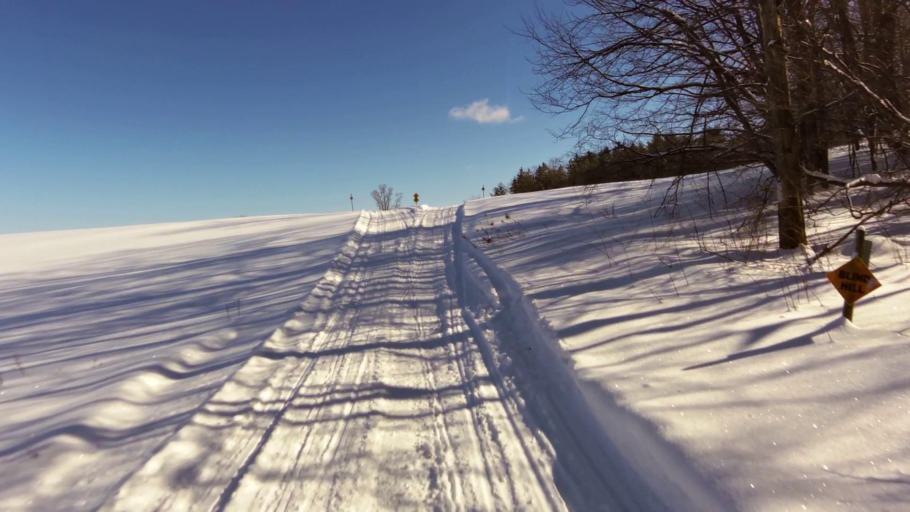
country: US
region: New York
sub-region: Chautauqua County
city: Fredonia
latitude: 42.3669
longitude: -79.1801
